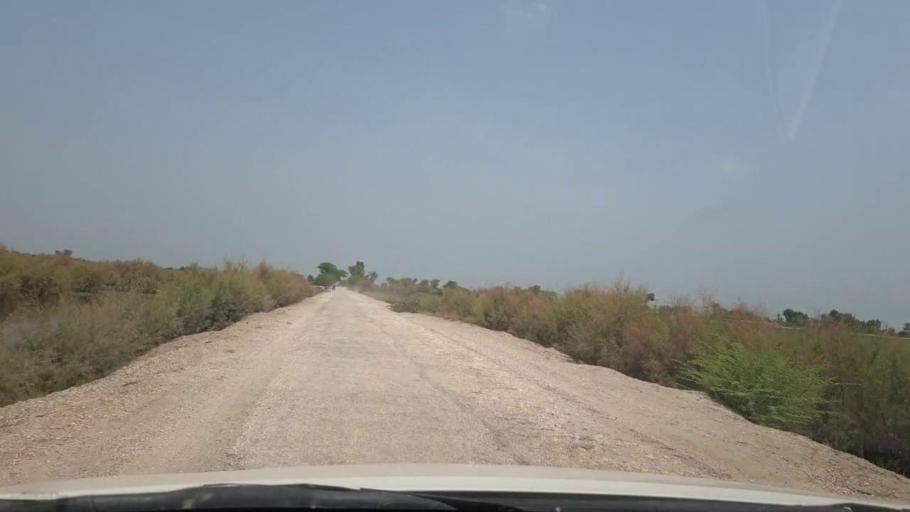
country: PK
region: Sindh
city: Rustam jo Goth
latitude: 28.0410
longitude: 68.8146
